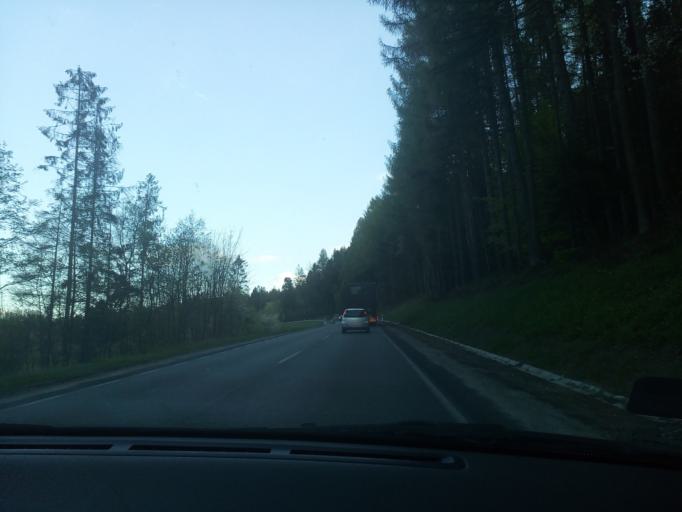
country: PL
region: Lesser Poland Voivodeship
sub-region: Powiat nowosadecki
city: Krynica-Zdroj
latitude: 49.4673
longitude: 20.9474
